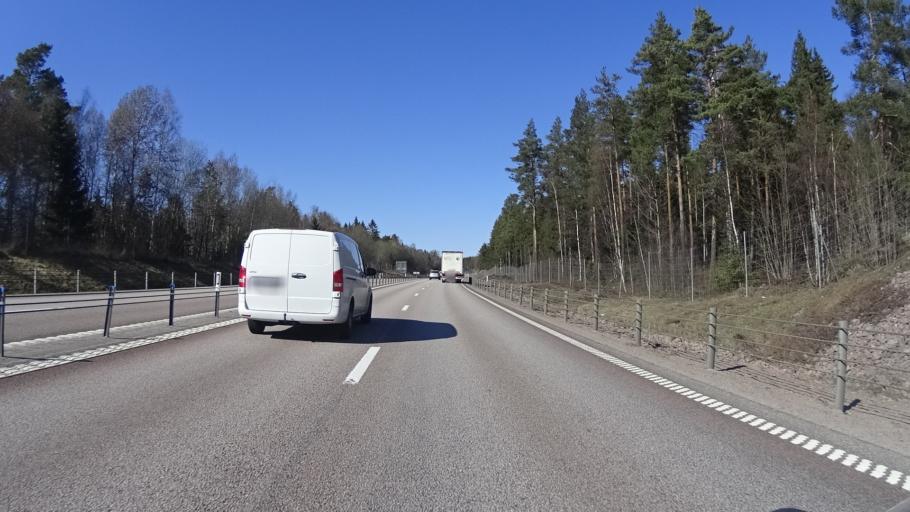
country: SE
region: Vaermland
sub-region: Kristinehamns Kommun
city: Kristinehamn
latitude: 59.3361
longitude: 14.0930
